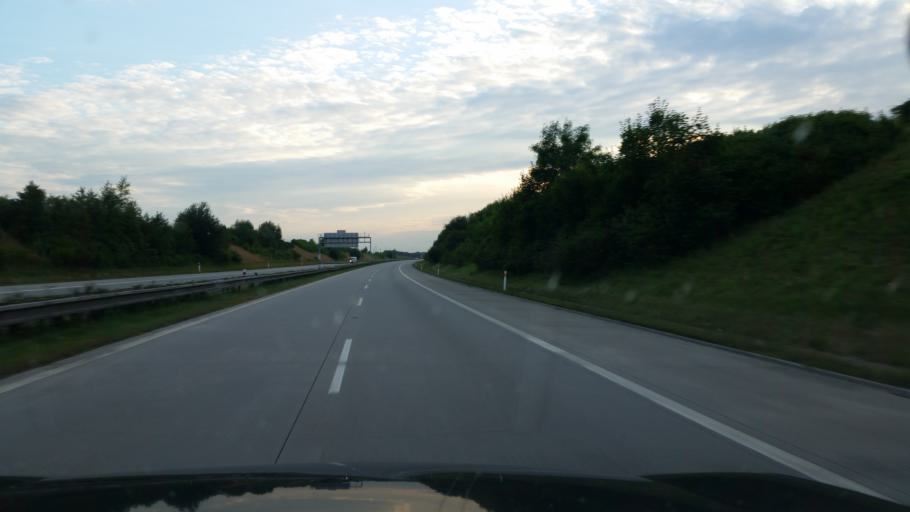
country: CZ
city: Klimkovice
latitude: 49.8023
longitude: 18.1912
